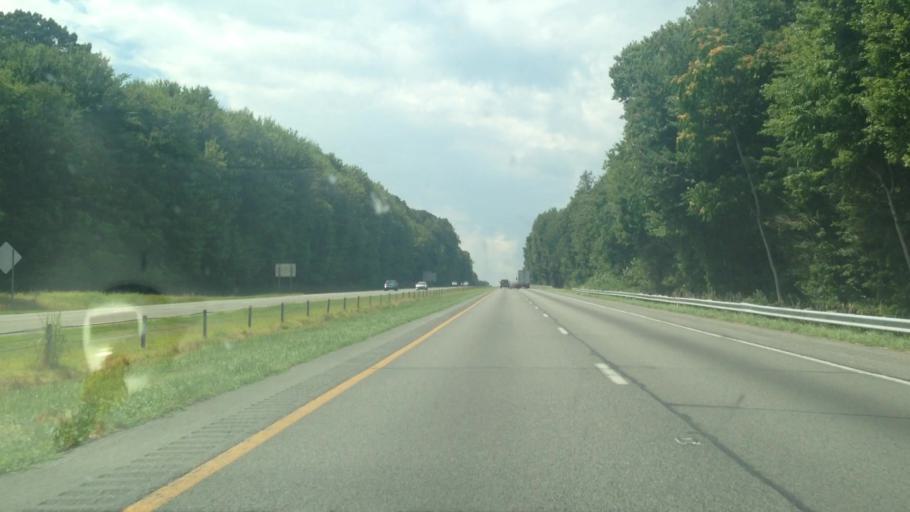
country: US
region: North Carolina
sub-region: Surry County
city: Pilot Mountain
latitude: 36.3440
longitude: -80.4612
